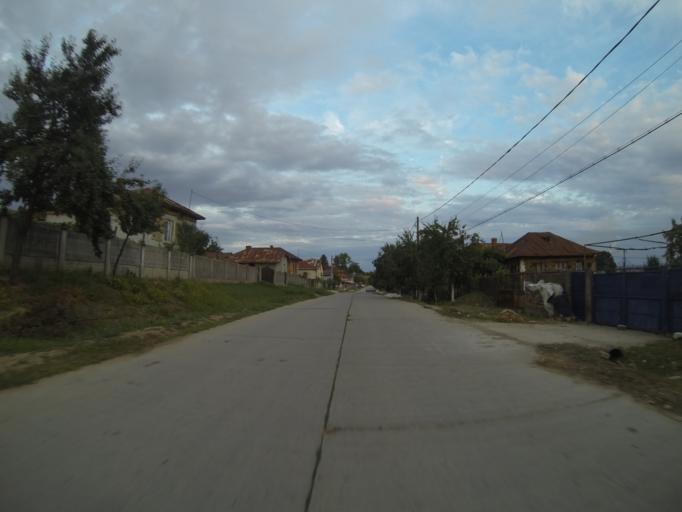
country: RO
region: Dolj
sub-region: Comuna Isalnita
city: Isalnita
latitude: 44.4229
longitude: 23.7195
